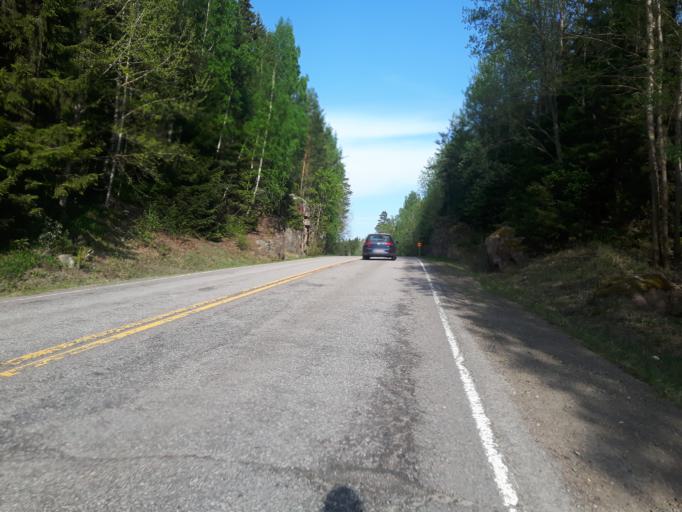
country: FI
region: Uusimaa
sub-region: Porvoo
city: Porvoo
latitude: 60.4822
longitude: 25.8299
